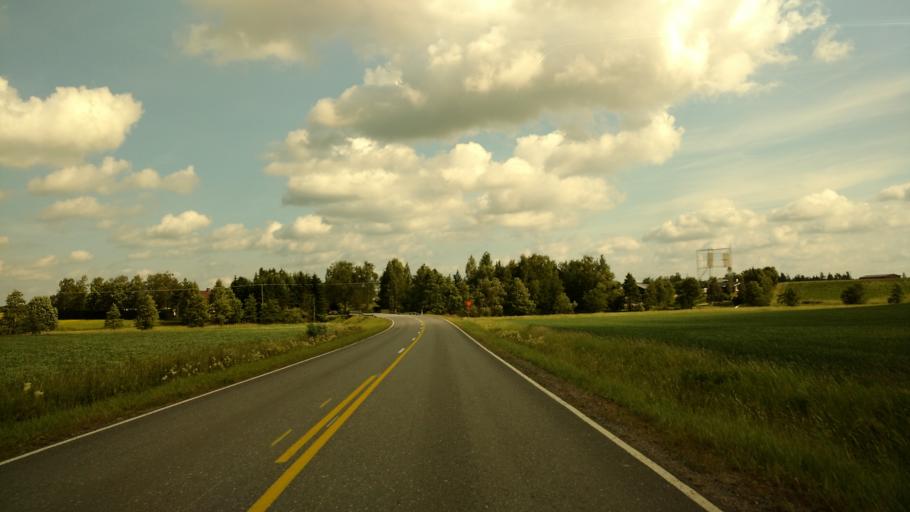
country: FI
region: Varsinais-Suomi
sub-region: Loimaa
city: Koski Tl
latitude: 60.6384
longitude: 23.1073
